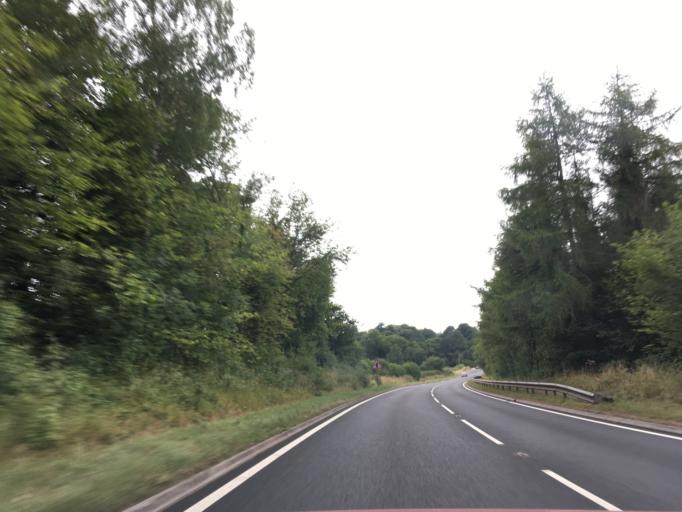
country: GB
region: Wales
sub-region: Sir Powys
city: Cray
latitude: 51.9496
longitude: -3.5205
